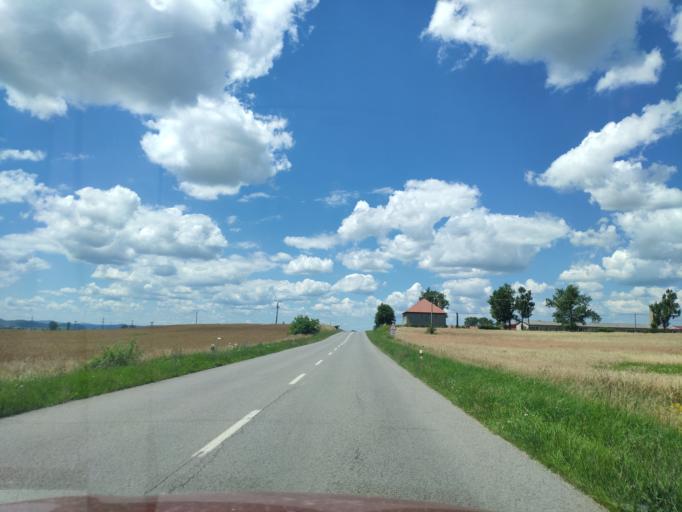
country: HU
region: Borsod-Abauj-Zemplen
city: Ozd
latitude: 48.3089
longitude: 20.2764
